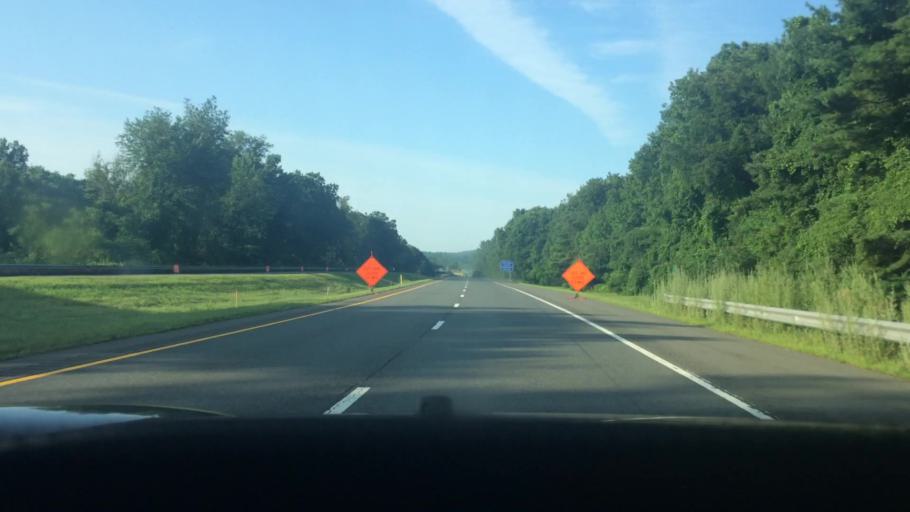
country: US
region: Massachusetts
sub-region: Franklin County
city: Greenfield
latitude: 42.6015
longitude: -72.6159
